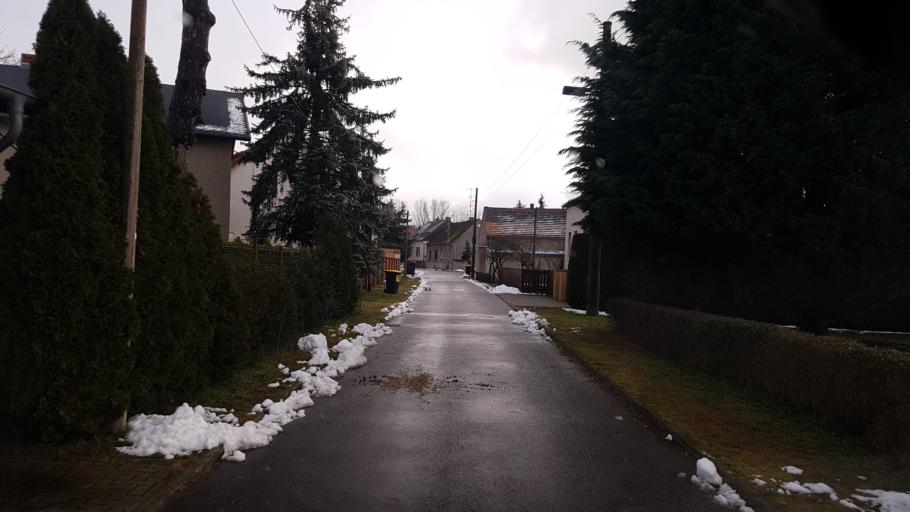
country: DE
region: Brandenburg
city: Forst
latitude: 51.8022
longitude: 14.5980
